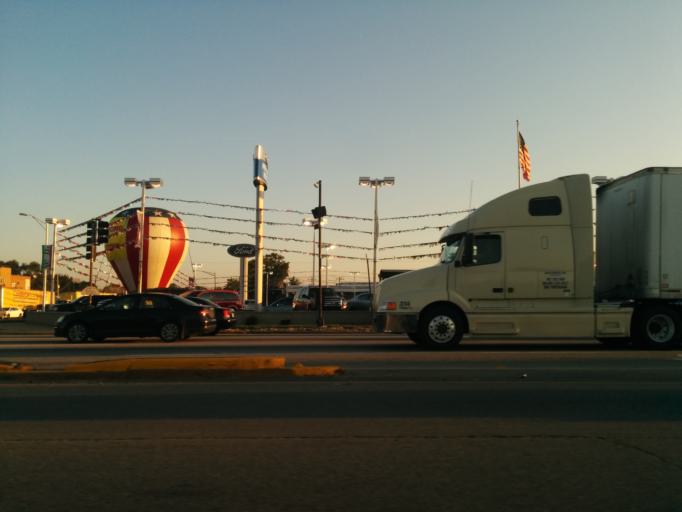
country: US
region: Illinois
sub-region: Cook County
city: Melrose Park
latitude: 41.9079
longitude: -87.8646
